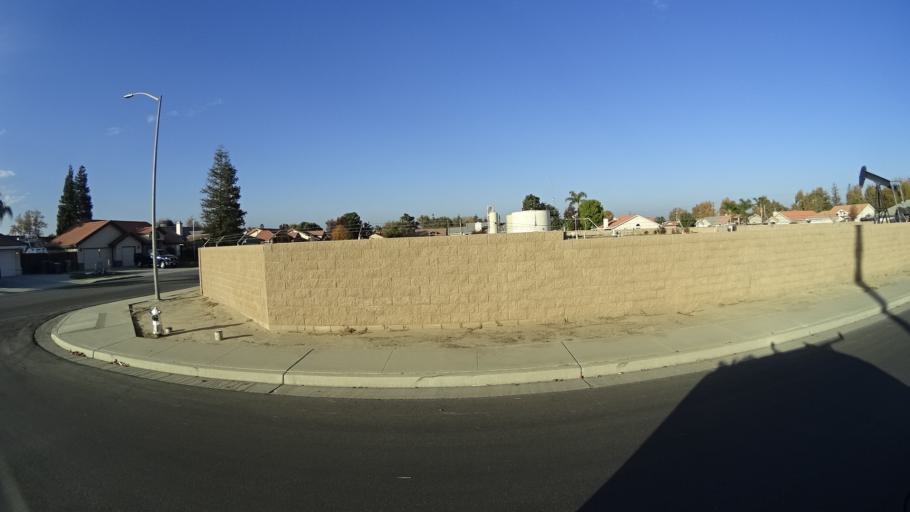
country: US
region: California
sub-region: Kern County
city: Rosedale
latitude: 35.3532
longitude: -119.1596
